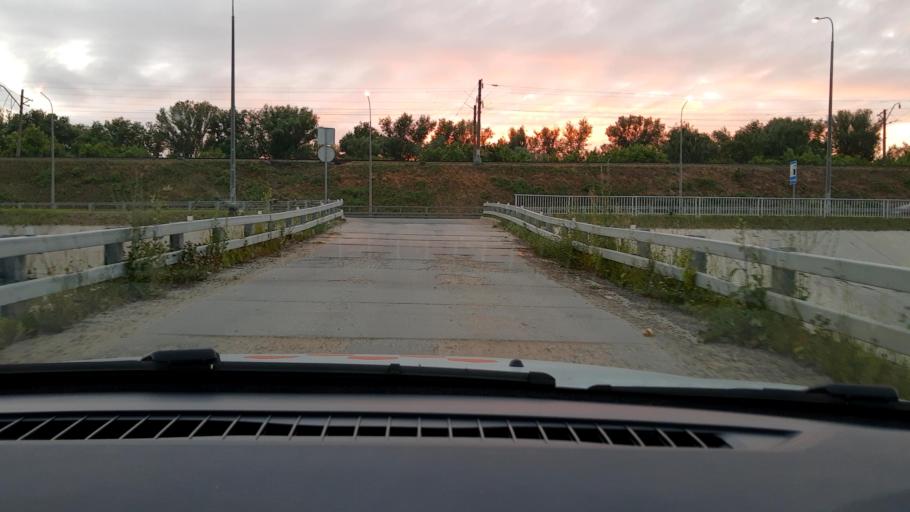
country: RU
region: Nizjnij Novgorod
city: Neklyudovo
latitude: 56.3653
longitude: 43.9376
